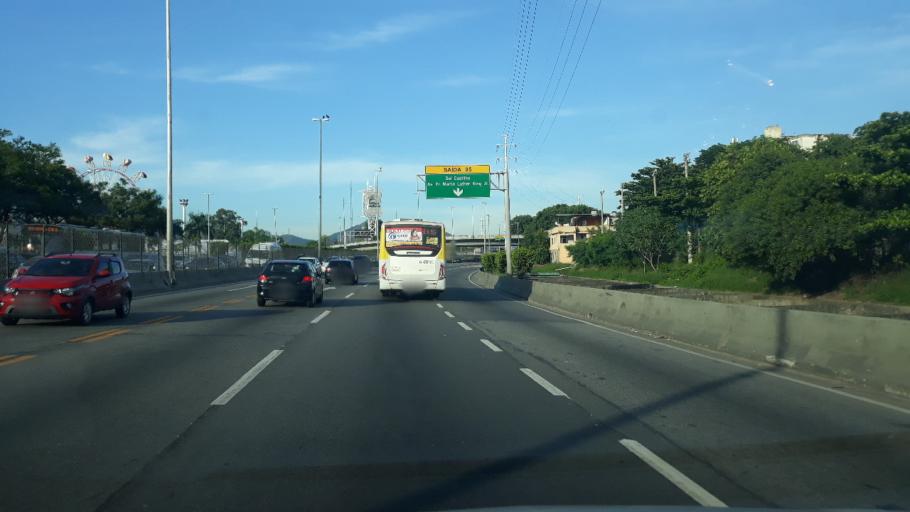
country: BR
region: Rio de Janeiro
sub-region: Rio De Janeiro
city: Rio de Janeiro
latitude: -22.8750
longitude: -43.2713
